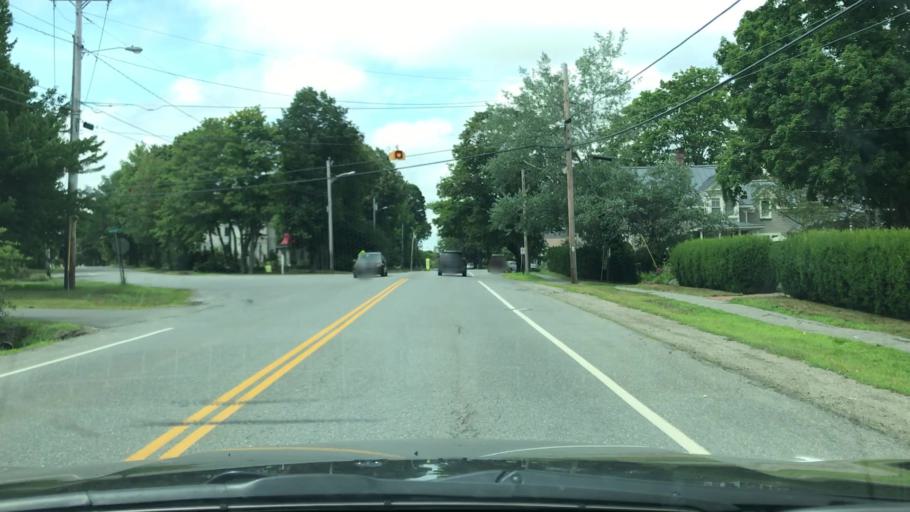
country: US
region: Maine
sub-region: Waldo County
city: Belfast
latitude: 44.4199
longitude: -68.9992
